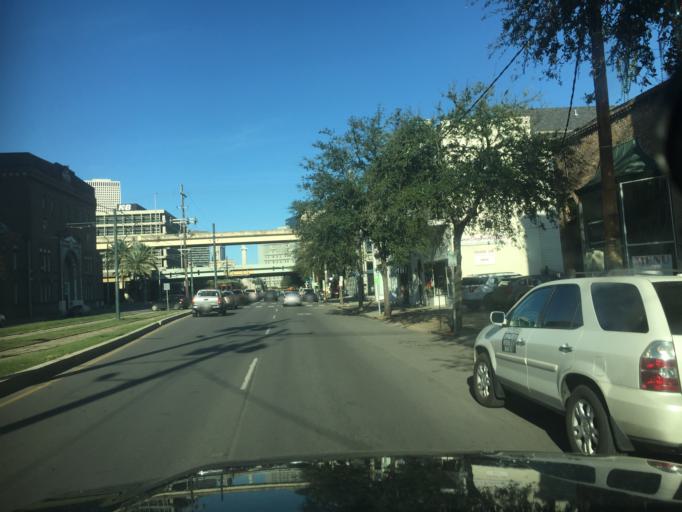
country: US
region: Louisiana
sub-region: Orleans Parish
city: New Orleans
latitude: 29.9408
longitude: -90.0741
